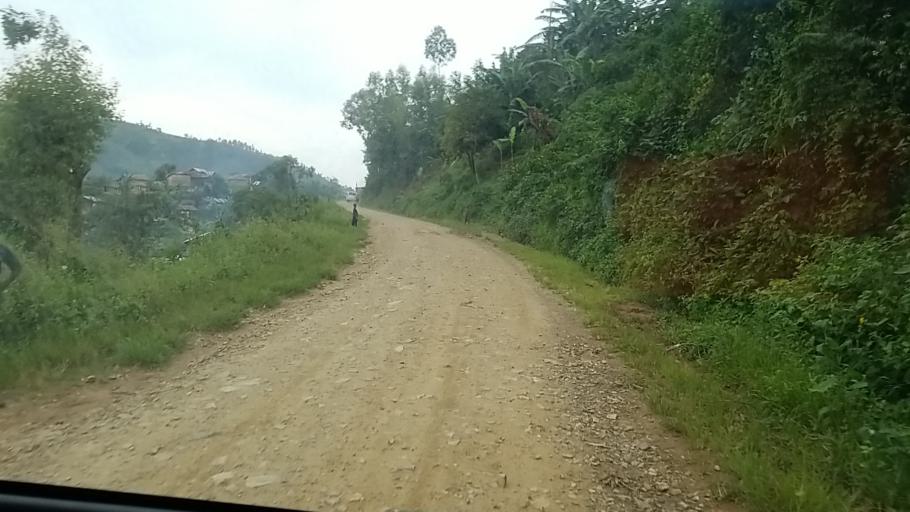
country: CD
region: Nord Kivu
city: Sake
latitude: -1.9570
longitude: 28.9204
